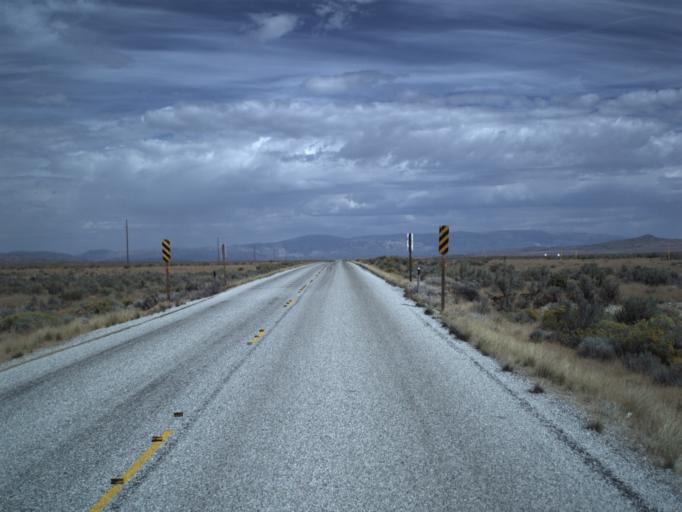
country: US
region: Utah
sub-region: Tooele County
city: Wendover
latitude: 41.5402
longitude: -113.5904
